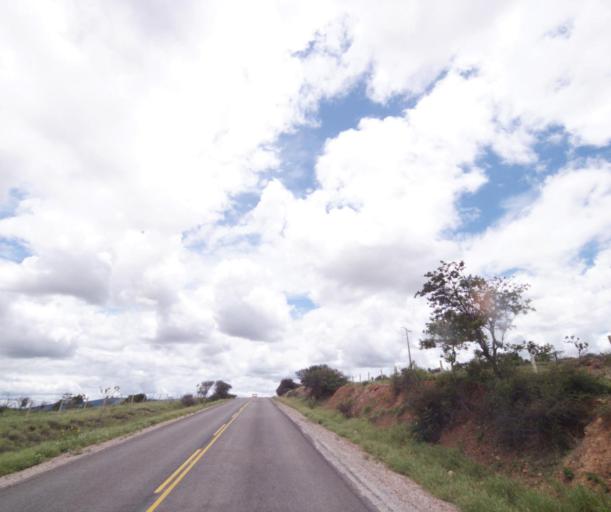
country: BR
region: Bahia
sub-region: Brumado
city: Brumado
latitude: -14.1538
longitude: -41.5138
